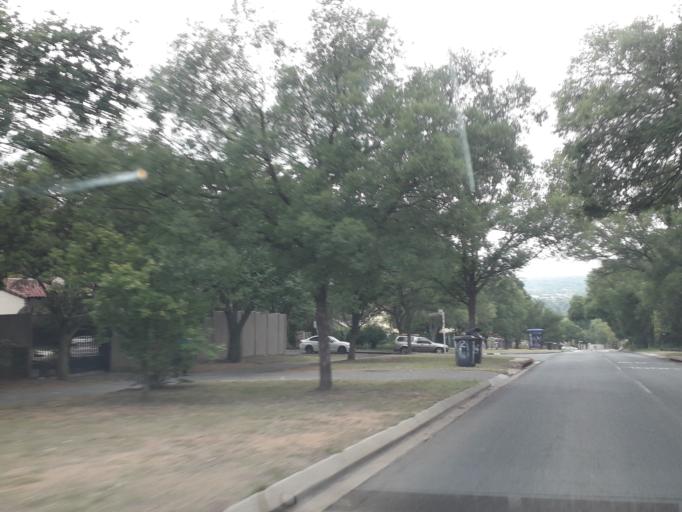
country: ZA
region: Gauteng
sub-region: City of Johannesburg Metropolitan Municipality
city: Roodepoort
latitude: -26.0976
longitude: 27.9581
